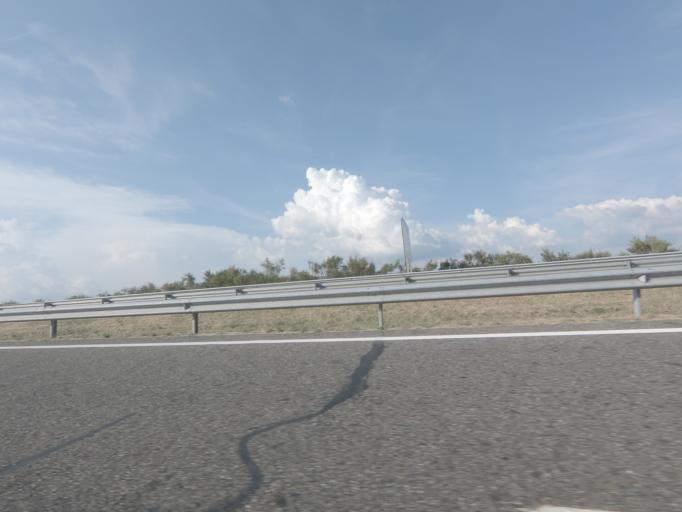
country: ES
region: Galicia
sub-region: Provincia de Ourense
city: Cualedro
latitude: 41.9760
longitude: -7.5329
